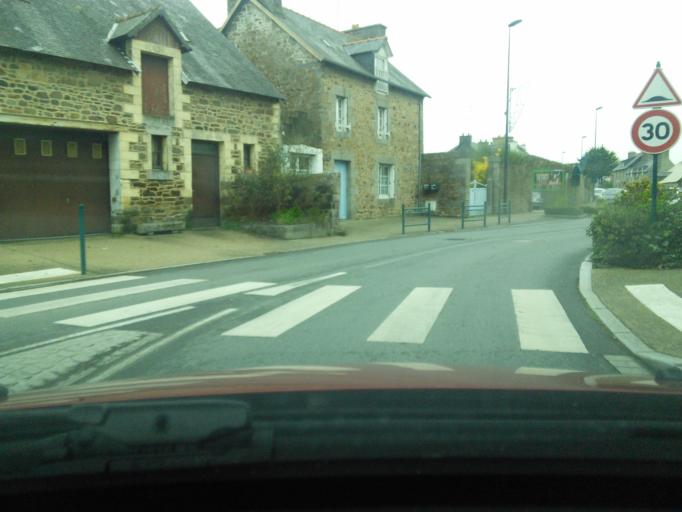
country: FR
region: Brittany
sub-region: Departement des Cotes-d'Armor
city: Yffiniac
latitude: 48.4850
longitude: -2.6765
